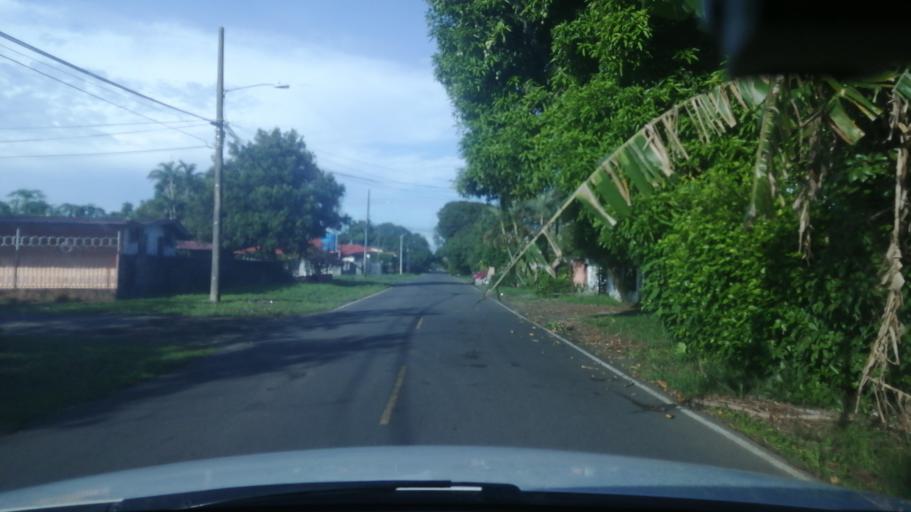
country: PA
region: Chiriqui
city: David
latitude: 8.4427
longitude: -82.4268
